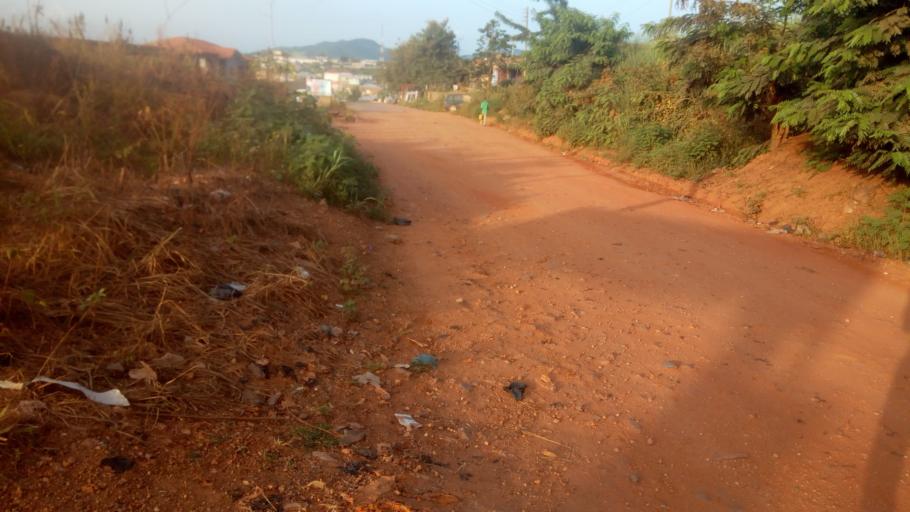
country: GH
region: Ashanti
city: Obuasi
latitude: 6.2127
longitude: -1.6993
